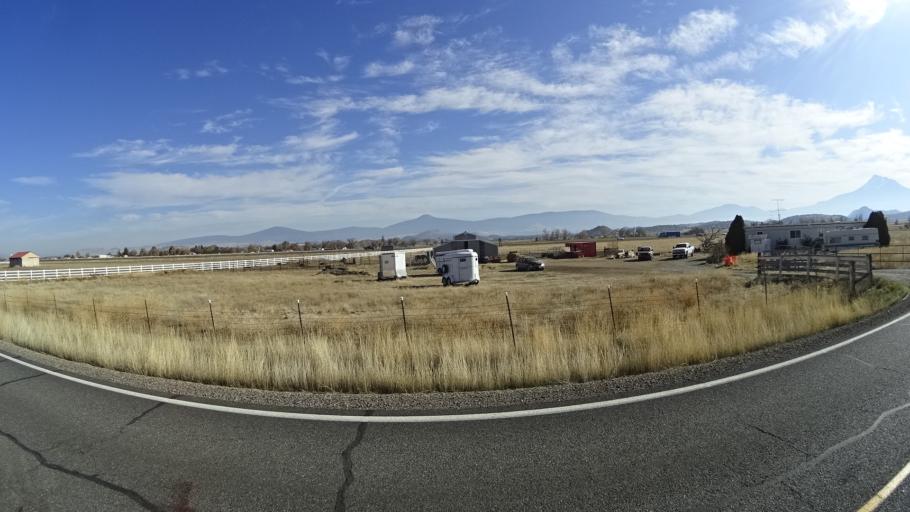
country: US
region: California
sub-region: Siskiyou County
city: Montague
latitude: 41.6367
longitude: -122.5316
